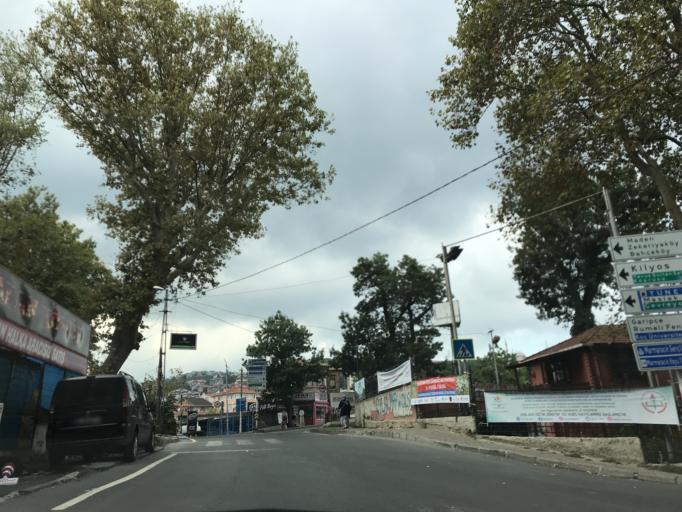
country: TR
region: Istanbul
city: Arikoey
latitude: 41.1720
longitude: 29.0534
